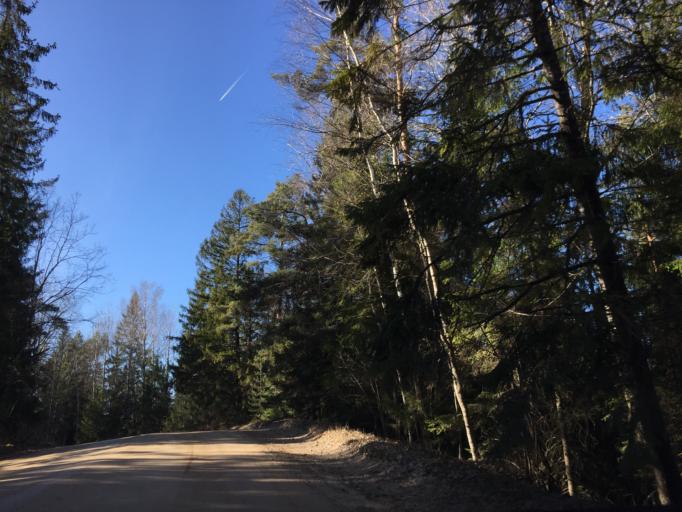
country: LV
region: Ropazu
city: Ropazi
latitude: 56.9194
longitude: 24.7382
